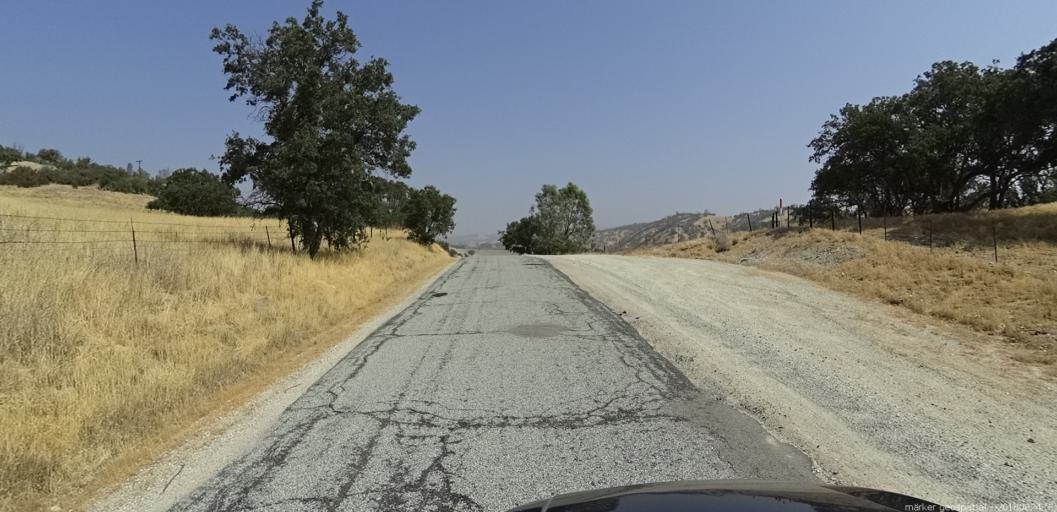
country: US
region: California
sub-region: San Luis Obispo County
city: San Miguel
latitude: 35.9717
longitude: -120.6473
